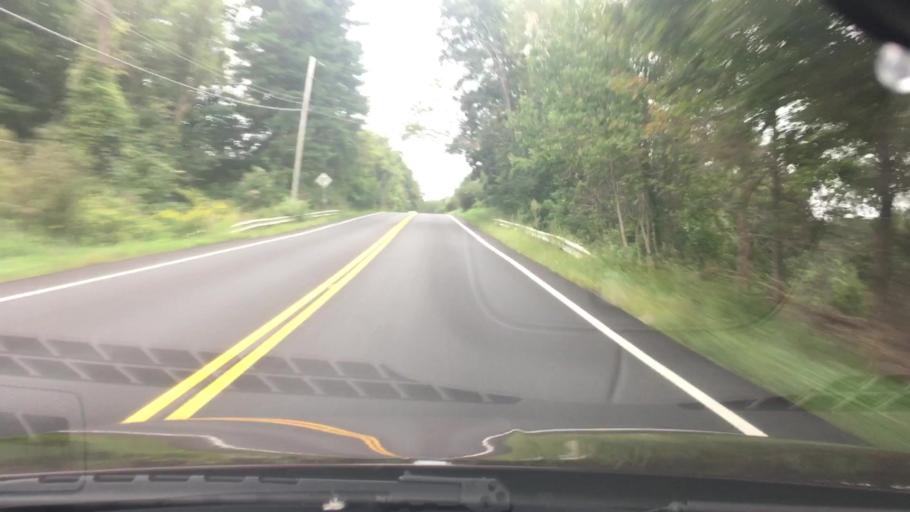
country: US
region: New York
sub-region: Dutchess County
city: Millbrook
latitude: 41.8372
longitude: -73.6115
